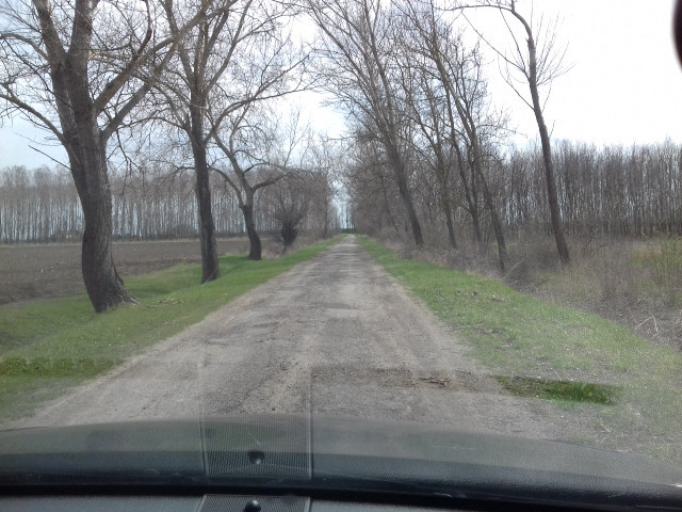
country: HU
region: Bacs-Kiskun
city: Tiszakecske
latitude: 46.9039
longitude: 20.1350
